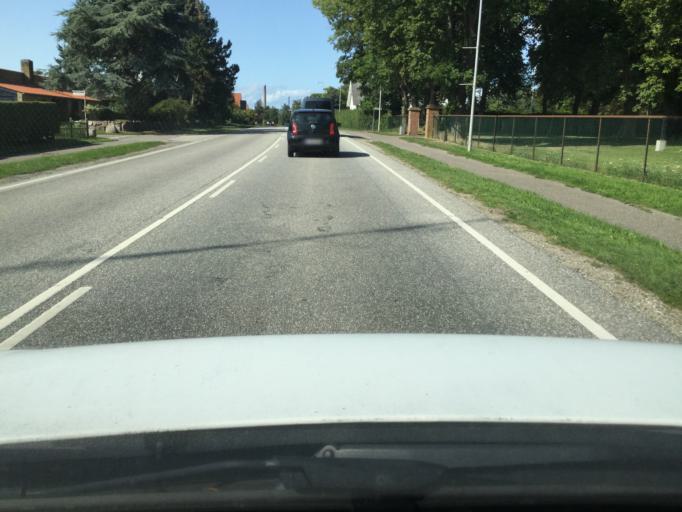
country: DK
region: Zealand
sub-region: Lolland Kommune
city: Nakskov
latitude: 54.8197
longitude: 11.1566
